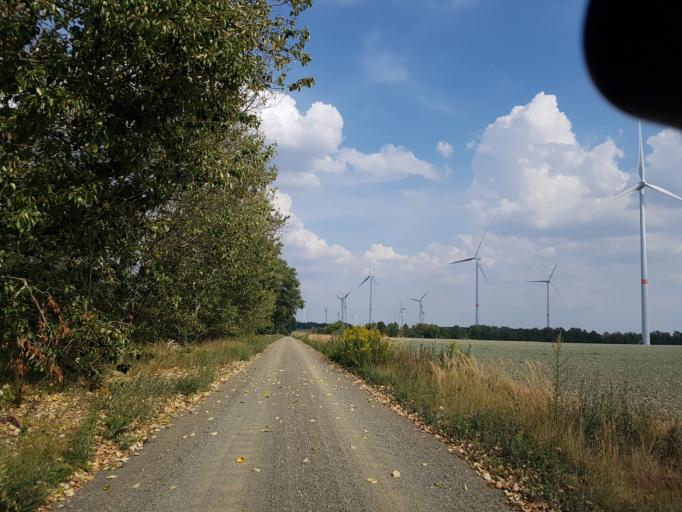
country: DE
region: Brandenburg
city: Treuenbrietzen
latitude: 52.0102
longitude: 12.8622
